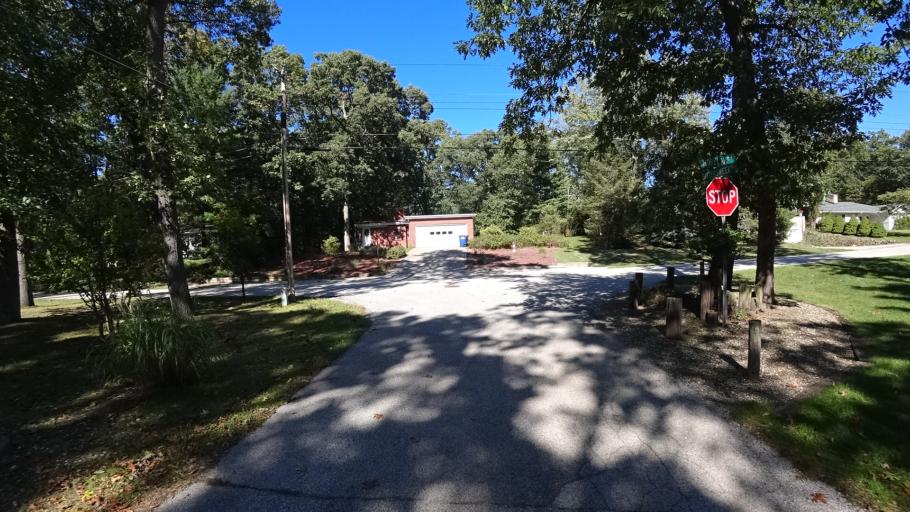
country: US
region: Indiana
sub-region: LaPorte County
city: Long Beach
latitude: 41.7527
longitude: -86.8304
